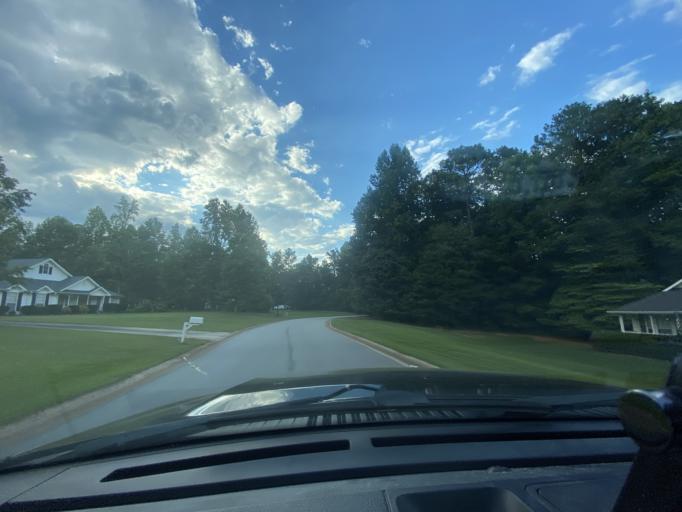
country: US
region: Georgia
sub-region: Fulton County
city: Palmetto
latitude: 33.4329
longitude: -84.6836
